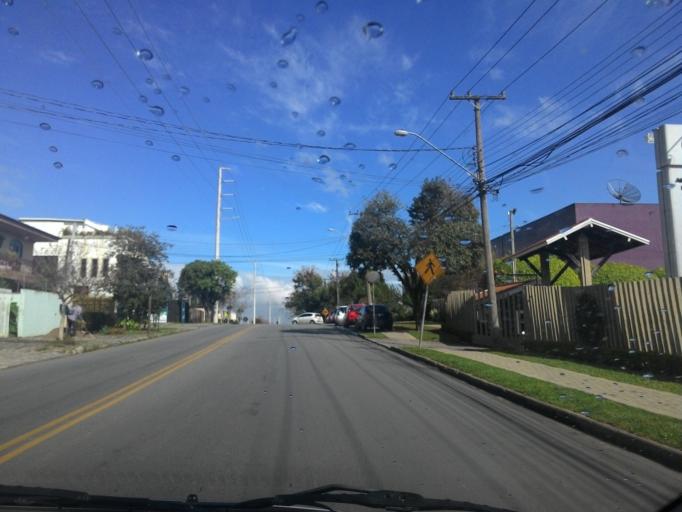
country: BR
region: Parana
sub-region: Pinhais
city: Pinhais
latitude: -25.4567
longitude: -49.2351
